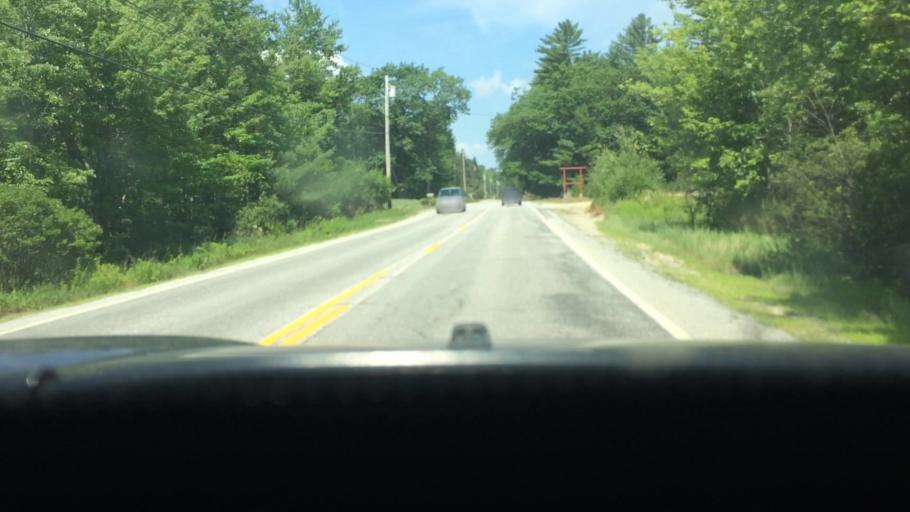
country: US
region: Maine
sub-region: Androscoggin County
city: Mechanic Falls
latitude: 44.1156
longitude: -70.4253
